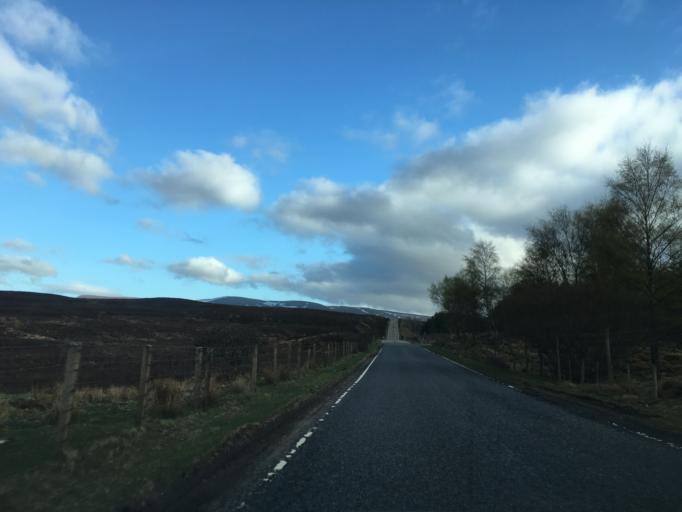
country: GB
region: Scotland
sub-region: Highland
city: Kingussie
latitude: 56.9820
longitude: -4.2375
